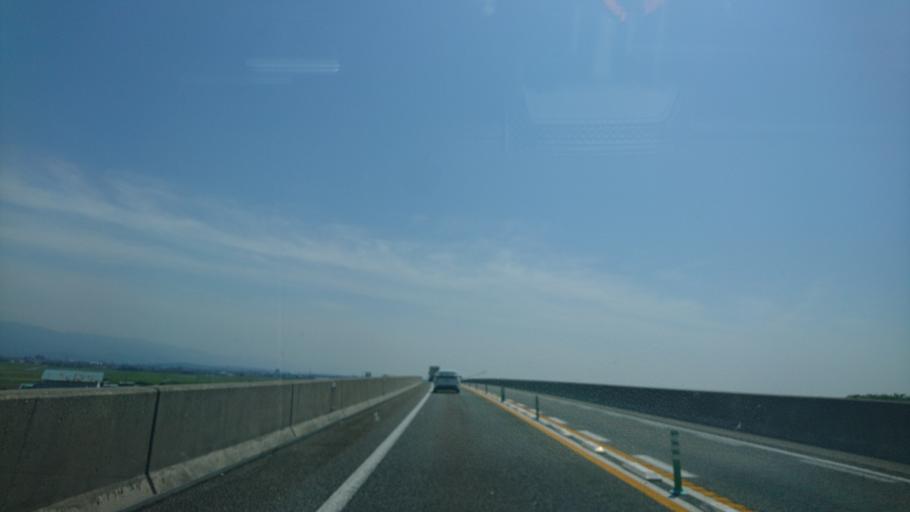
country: JP
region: Niigata
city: Shibata
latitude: 37.9865
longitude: 139.3159
